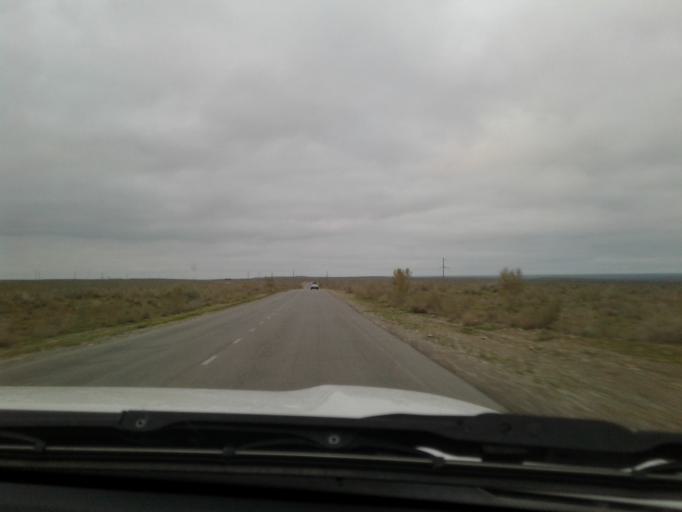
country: TM
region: Lebap
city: Farap
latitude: 39.0873
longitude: 63.7238
